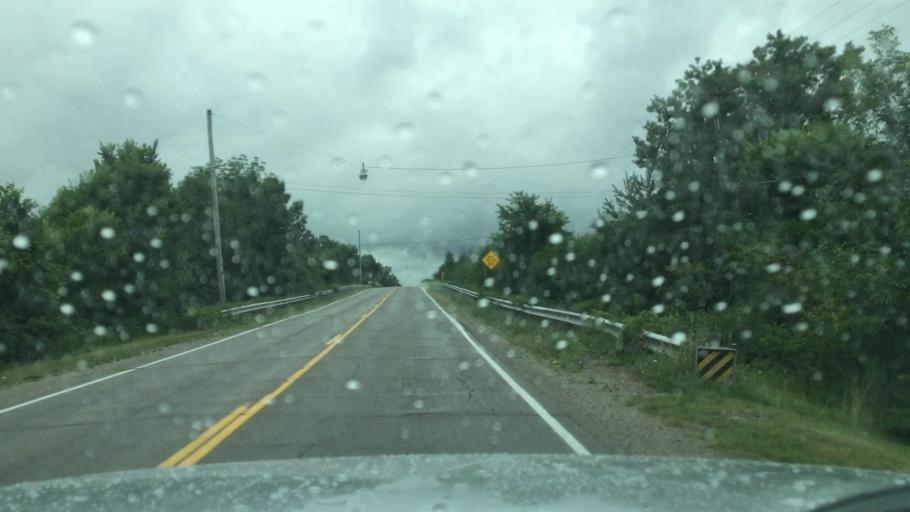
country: US
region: Michigan
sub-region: Genesee County
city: Beecher
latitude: 43.0753
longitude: -83.7604
